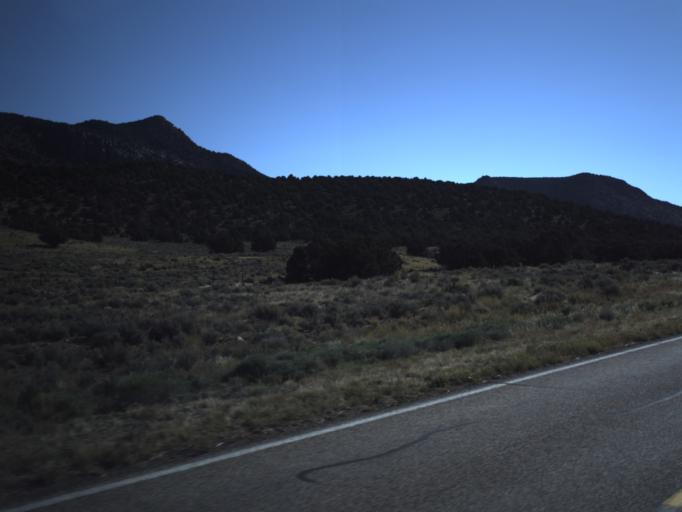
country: US
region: Utah
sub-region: Washington County
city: Enterprise
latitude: 37.6725
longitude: -113.4886
